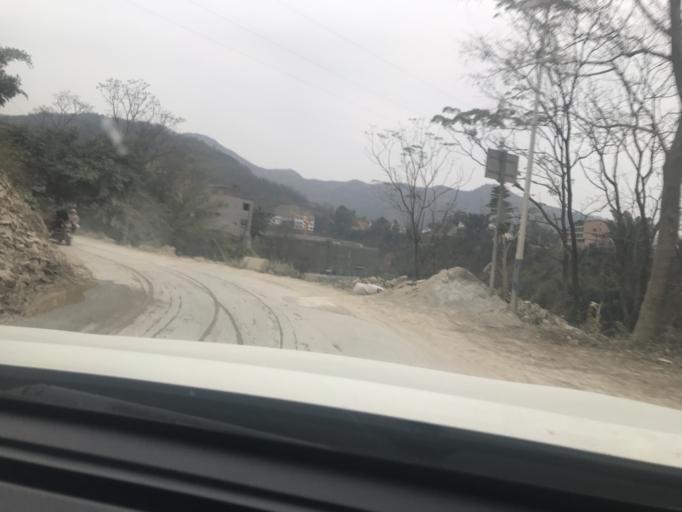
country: CN
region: Guangxi Zhuangzu Zizhiqu
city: Xinzhou
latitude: 24.9857
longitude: 105.8203
